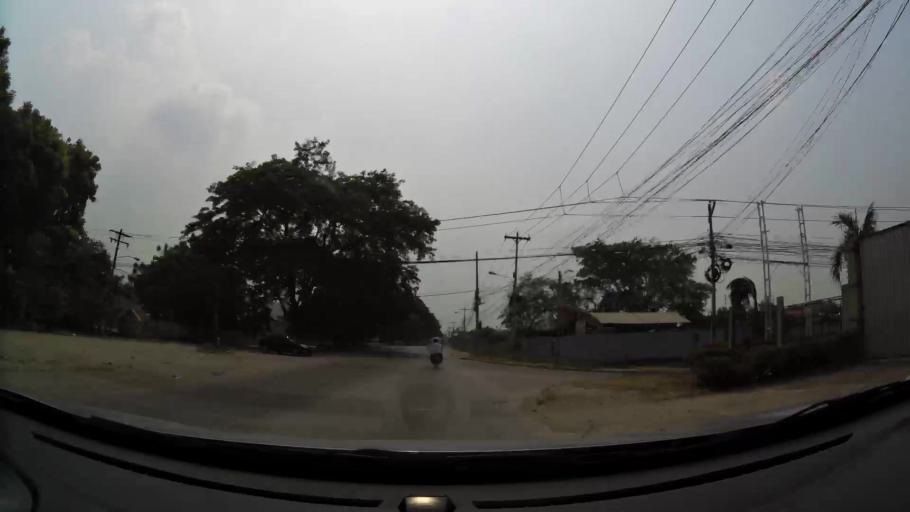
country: HN
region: Cortes
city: Chotepe
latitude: 15.4658
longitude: -87.9758
